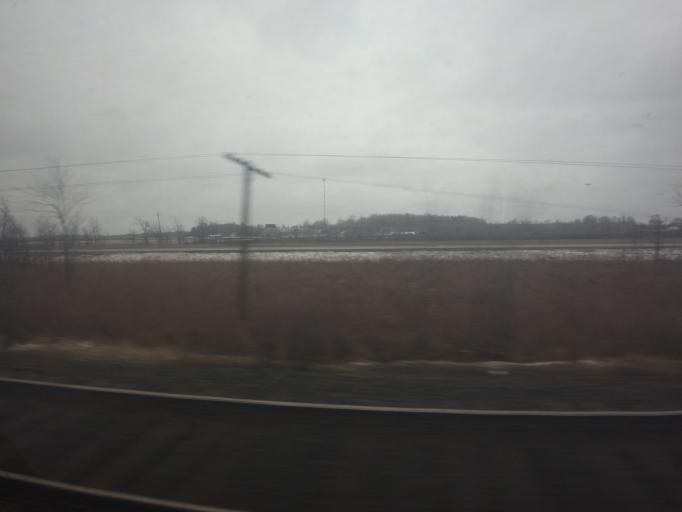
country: CA
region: Ontario
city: Kingston
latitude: 44.3197
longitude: -76.3625
